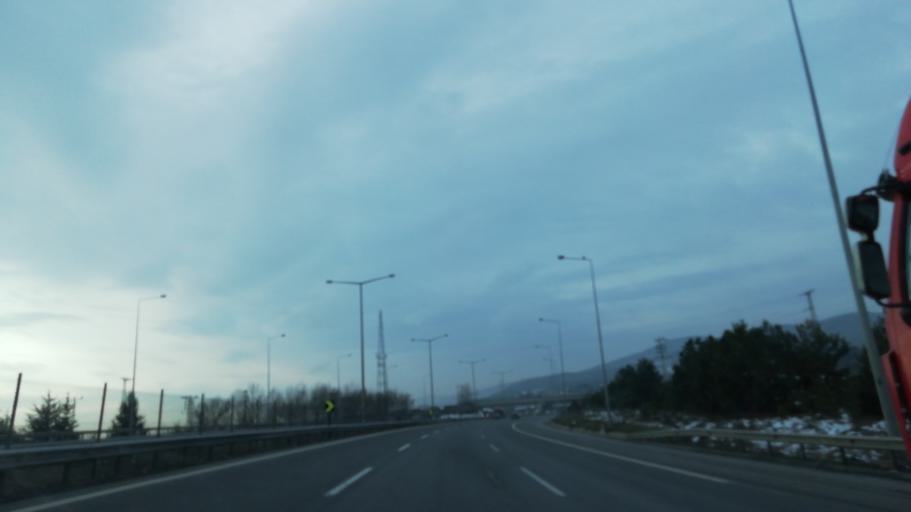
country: TR
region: Bolu
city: Bolu
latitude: 40.7657
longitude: 31.6370
